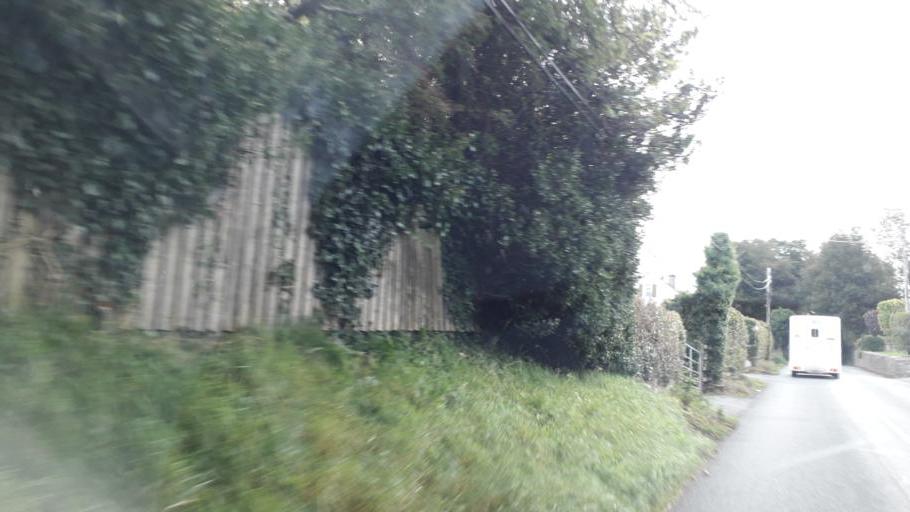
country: IE
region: Leinster
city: Foxrock
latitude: 53.2312
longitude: -6.1999
